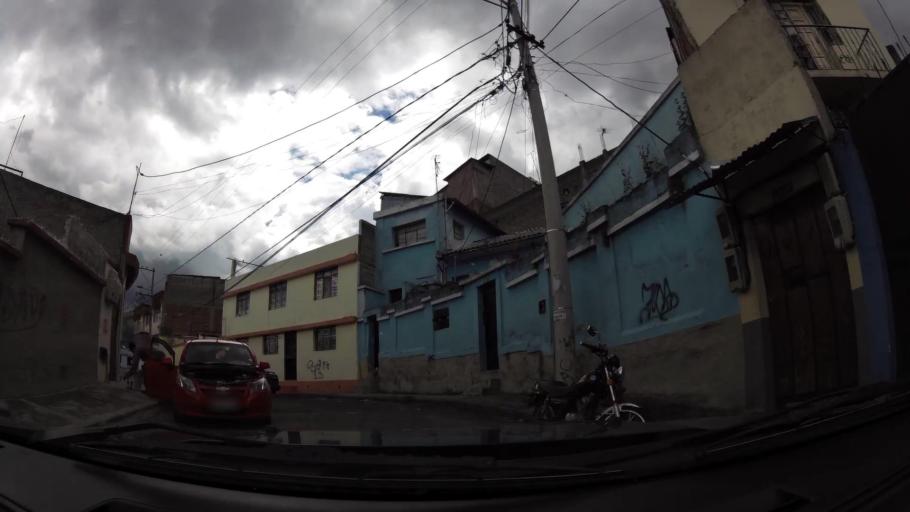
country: EC
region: Pichincha
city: Quito
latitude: -0.2500
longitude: -78.5135
